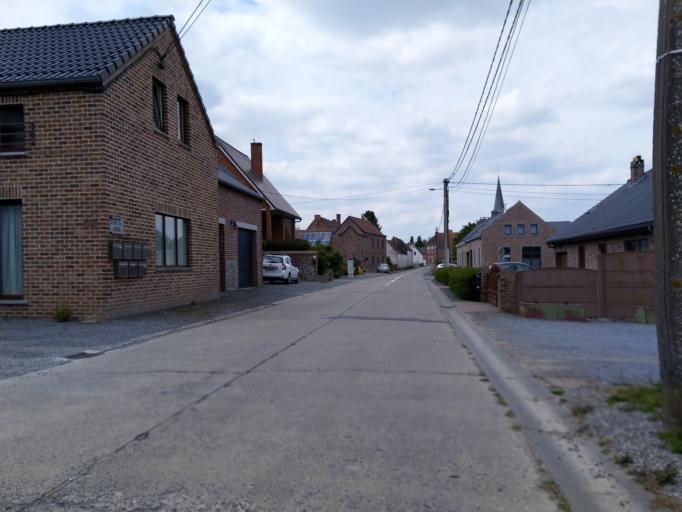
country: BE
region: Wallonia
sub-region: Province du Hainaut
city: Lens
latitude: 50.5811
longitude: 3.9190
